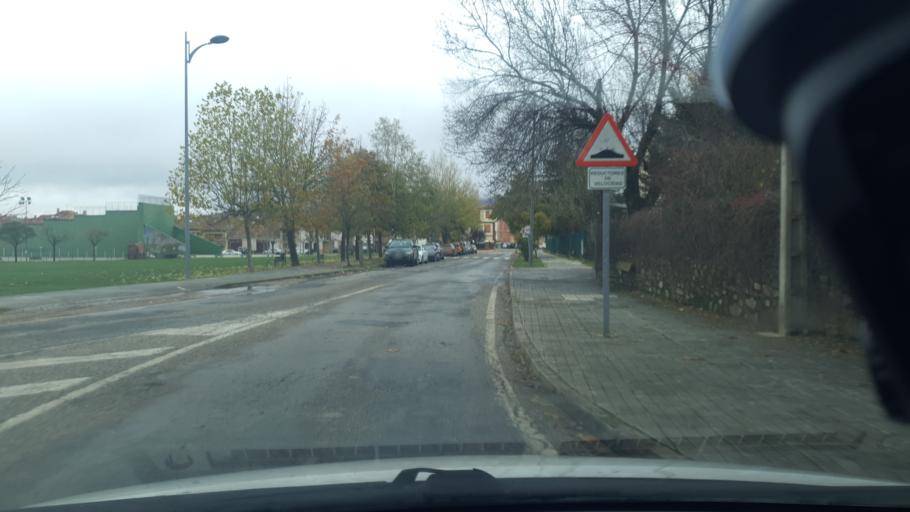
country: ES
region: Castille and Leon
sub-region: Provincia de Segovia
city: Riaza
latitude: 41.2767
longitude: -3.4821
